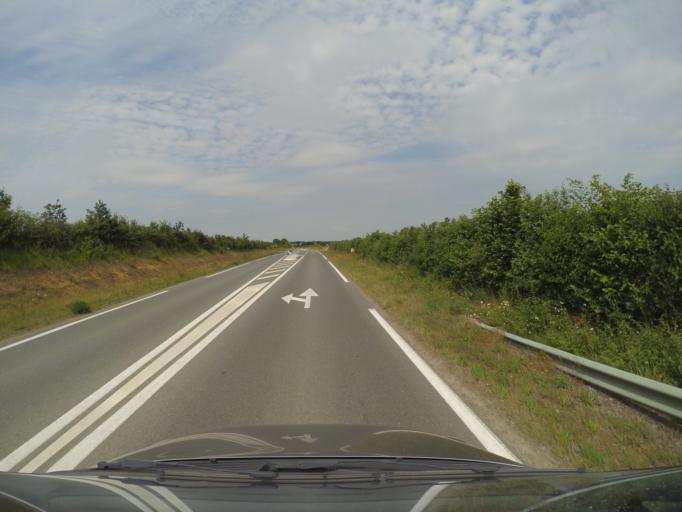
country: FR
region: Pays de la Loire
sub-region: Departement de la Vendee
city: Les Herbiers
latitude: 46.8476
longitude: -1.0326
